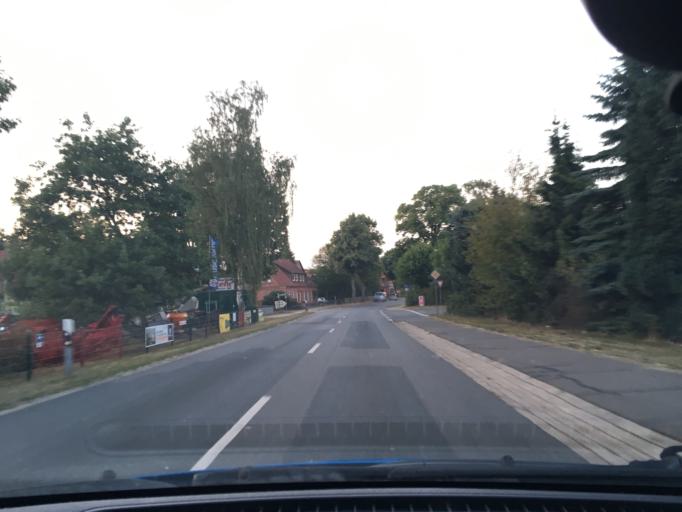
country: DE
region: Lower Saxony
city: Embsen
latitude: 53.1733
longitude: 10.3446
